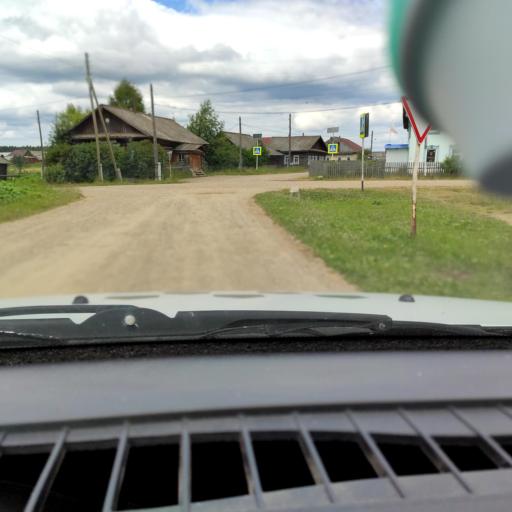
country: RU
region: Perm
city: Suksun
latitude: 57.2133
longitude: 57.6993
